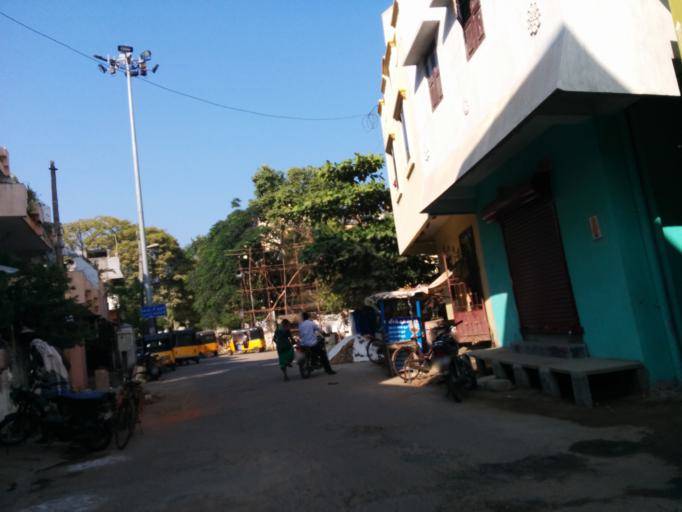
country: IN
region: Pondicherry
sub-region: Puducherry
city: Puducherry
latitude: 11.9449
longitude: 79.8341
